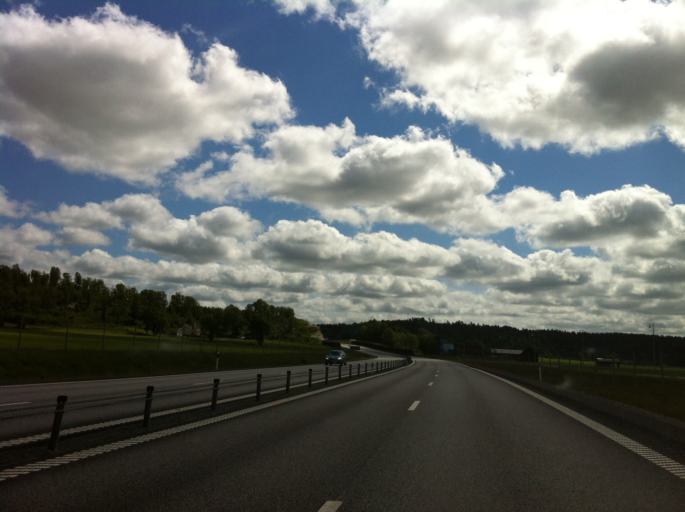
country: SE
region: Vaestra Goetaland
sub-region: Lilla Edets Kommun
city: Lodose
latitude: 58.0030
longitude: 12.1596
